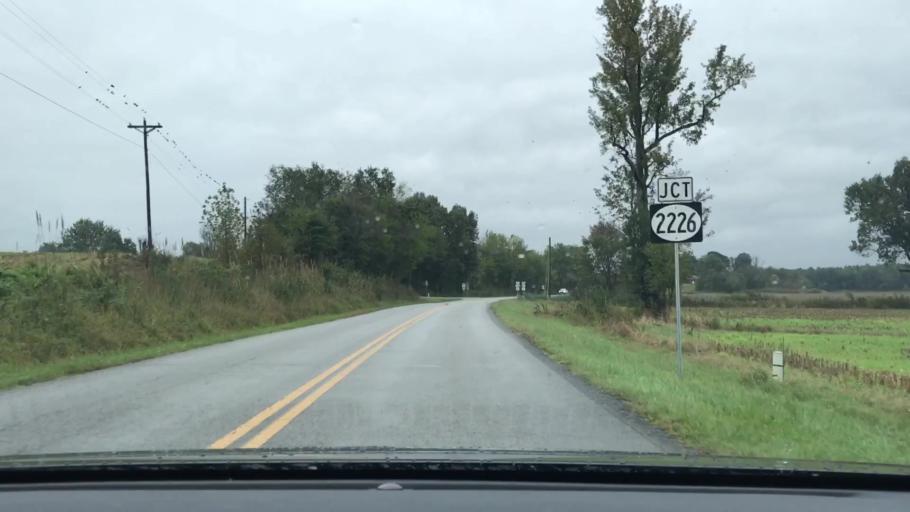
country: US
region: Kentucky
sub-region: McLean County
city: Calhoun
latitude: 37.4665
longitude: -87.2326
